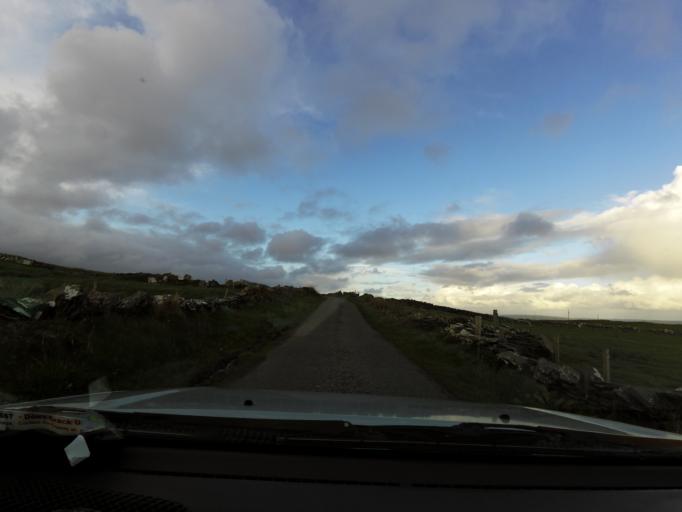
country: IE
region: Munster
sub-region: An Clar
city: Kilrush
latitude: 52.9509
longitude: -9.4432
